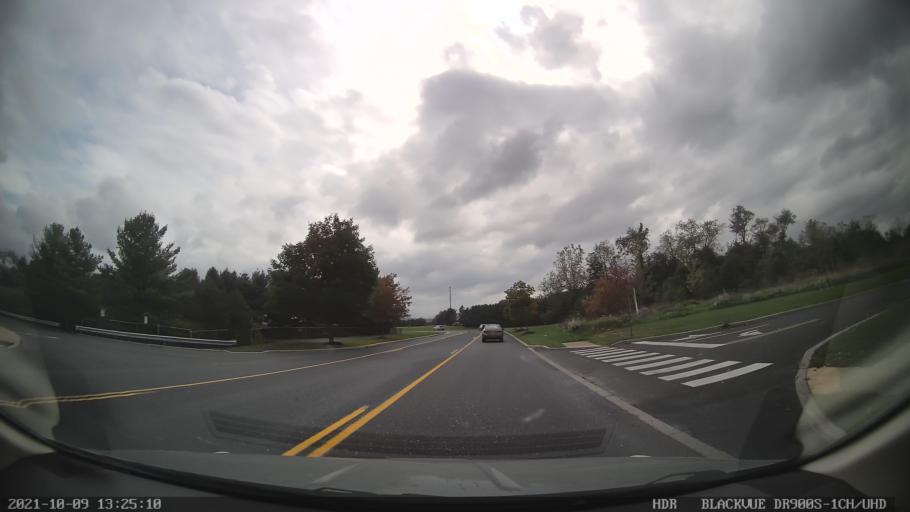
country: US
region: Pennsylvania
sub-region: Lehigh County
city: Ancient Oaks
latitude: 40.5520
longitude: -75.5809
